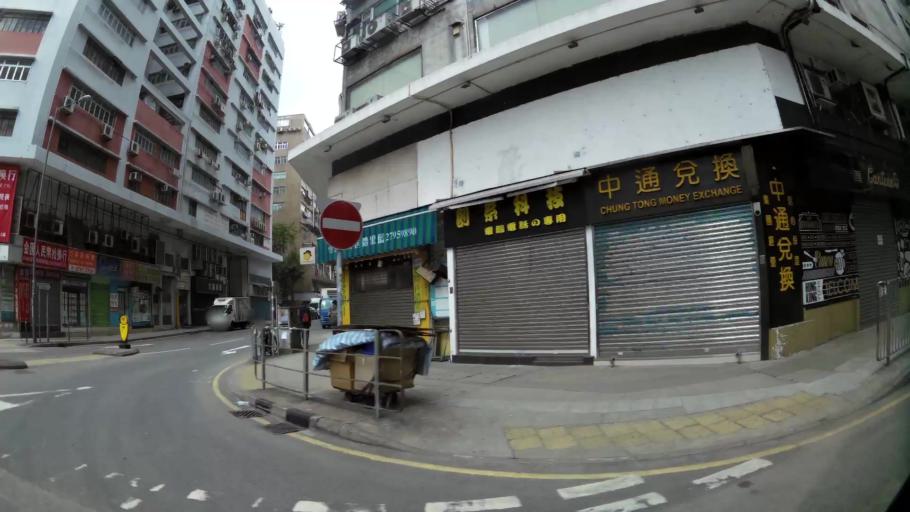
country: HK
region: Kowloon City
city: Kowloon
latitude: 22.3234
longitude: 114.2108
